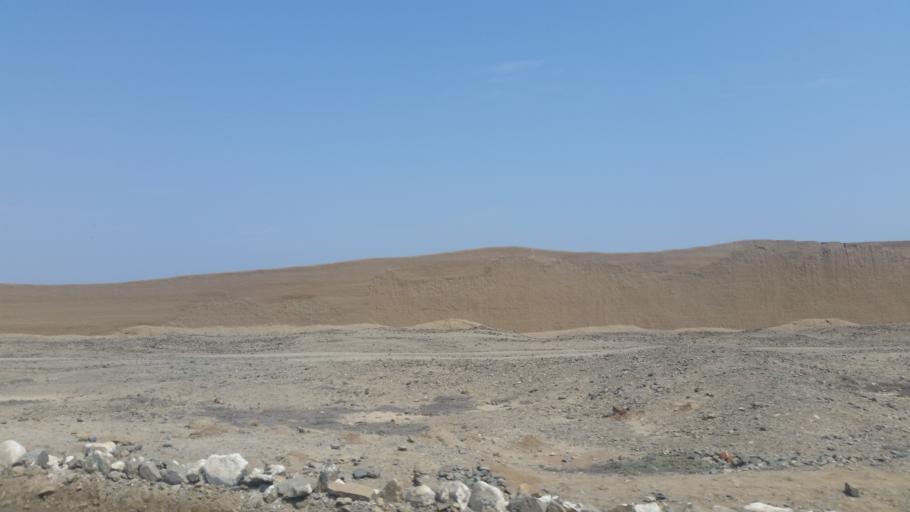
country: PE
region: La Libertad
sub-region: Provincia de Trujillo
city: La Esperanza
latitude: -8.1023
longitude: -79.0725
